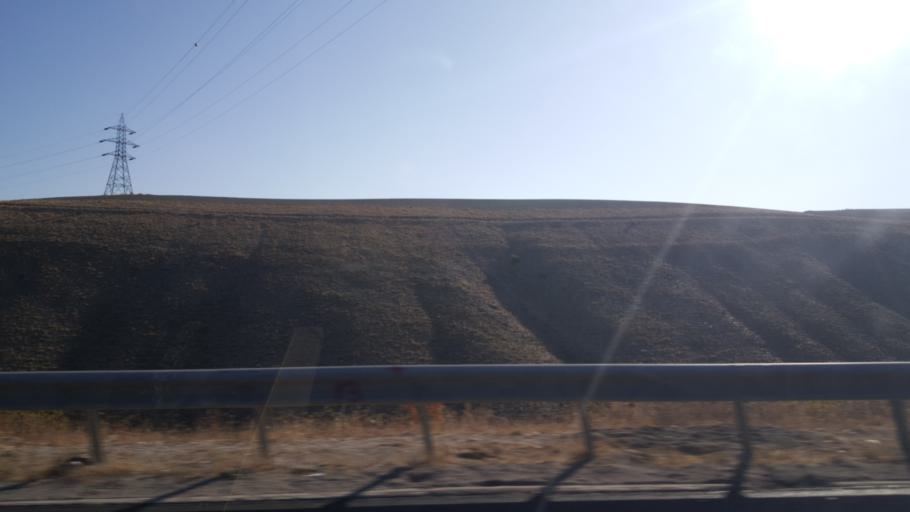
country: TR
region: Ankara
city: Cankaya
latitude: 39.8507
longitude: 32.8929
